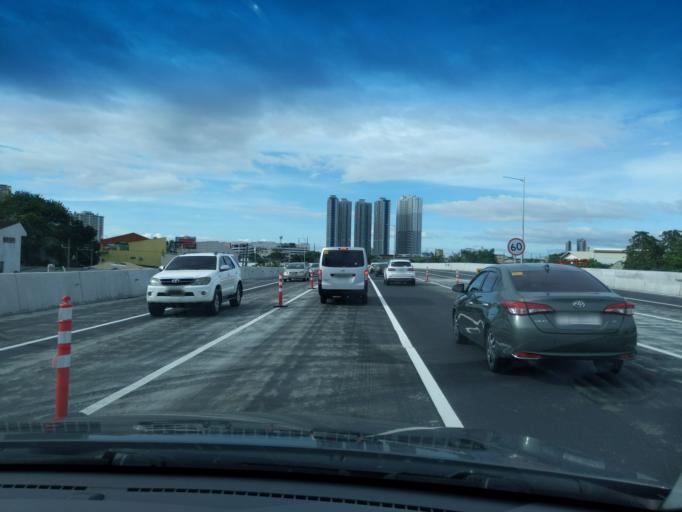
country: PH
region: Metro Manila
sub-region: San Juan
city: San Juan
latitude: 14.5987
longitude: 121.0240
